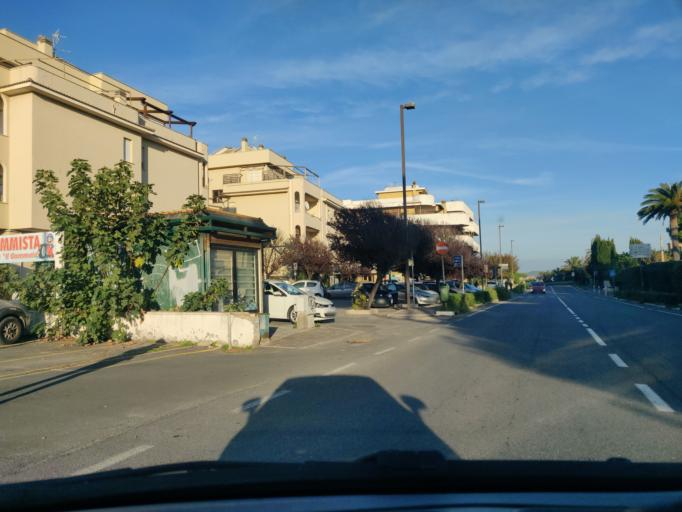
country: IT
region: Latium
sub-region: Citta metropolitana di Roma Capitale
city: Santa Marinella
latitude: 42.0386
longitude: 11.8789
